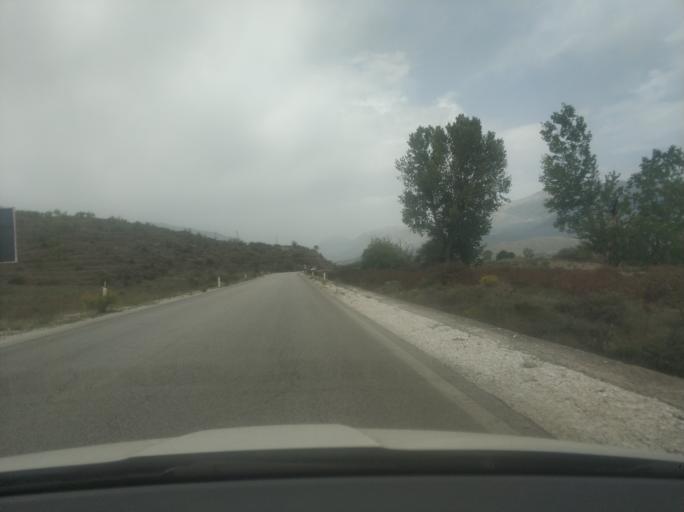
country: AL
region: Gjirokaster
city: Gjirokaster
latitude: 40.1056
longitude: 20.1231
